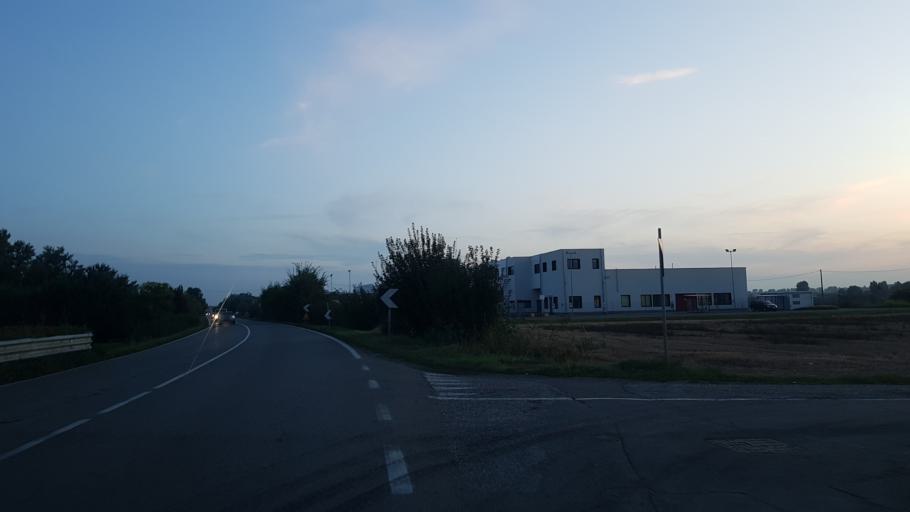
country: IT
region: Emilia-Romagna
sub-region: Provincia di Modena
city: San Prospero
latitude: 44.8046
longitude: 11.0283
